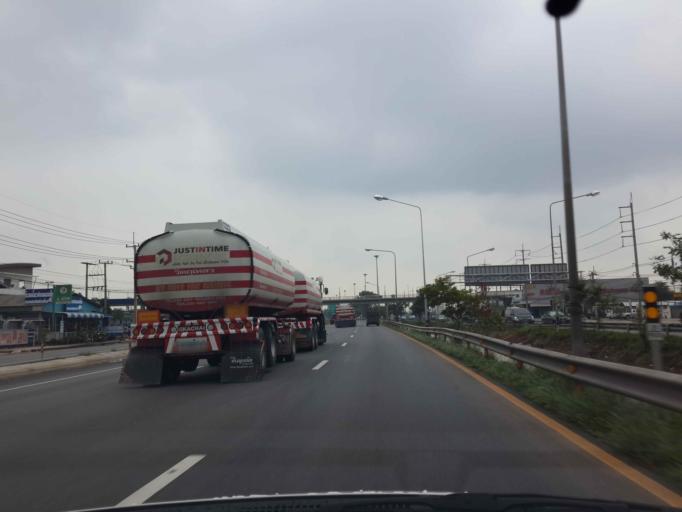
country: TH
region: Samut Sakhon
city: Samut Sakhon
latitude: 13.5861
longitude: 100.3202
